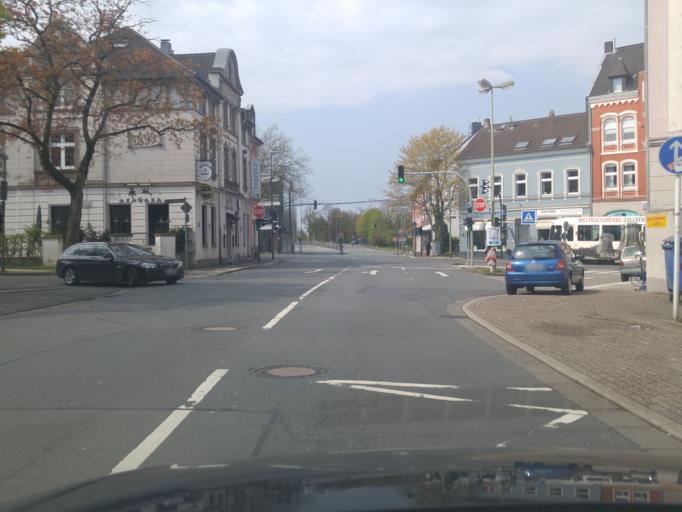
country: DE
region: North Rhine-Westphalia
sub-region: Regierungsbezirk Dusseldorf
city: Essen
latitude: 51.4136
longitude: 6.9952
